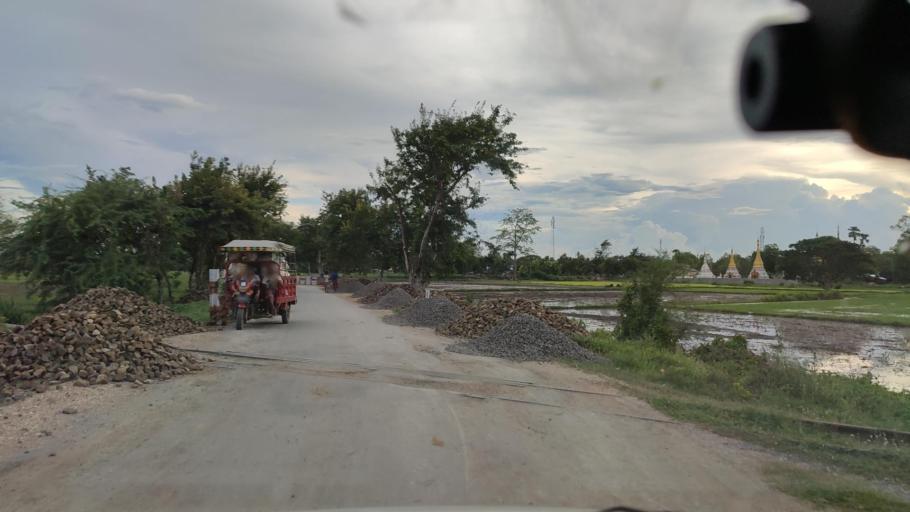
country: MM
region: Magway
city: Minbu
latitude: 20.3113
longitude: 94.7563
